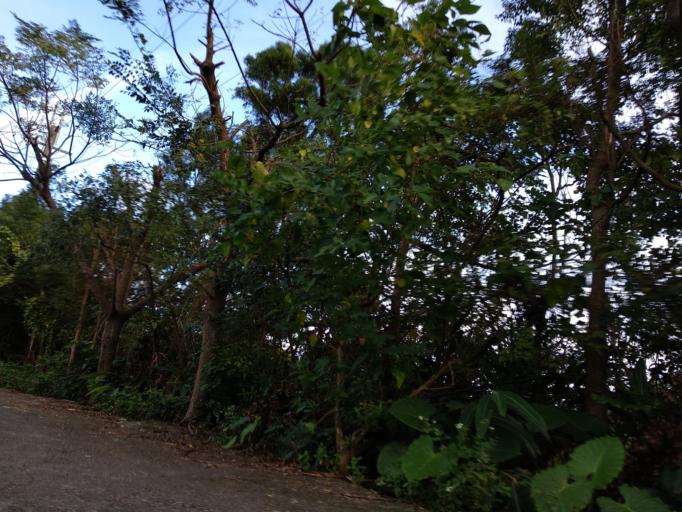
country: TW
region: Taiwan
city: Daxi
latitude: 24.9304
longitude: 121.1886
